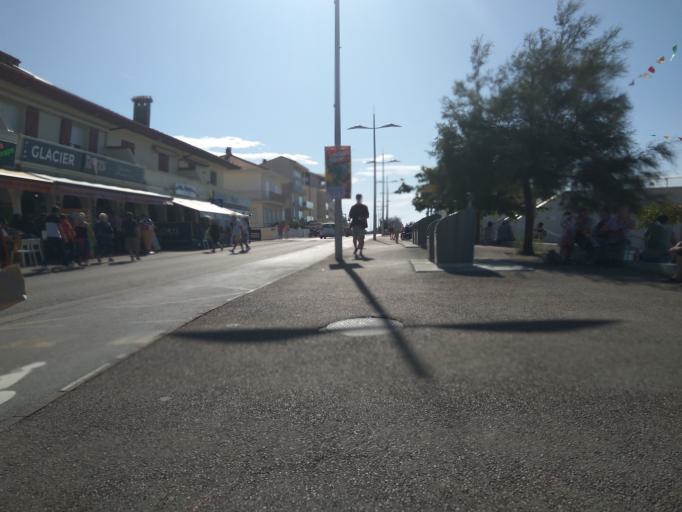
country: FR
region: Aquitaine
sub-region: Departement des Landes
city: Capbreton
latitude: 43.6540
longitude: -1.4449
